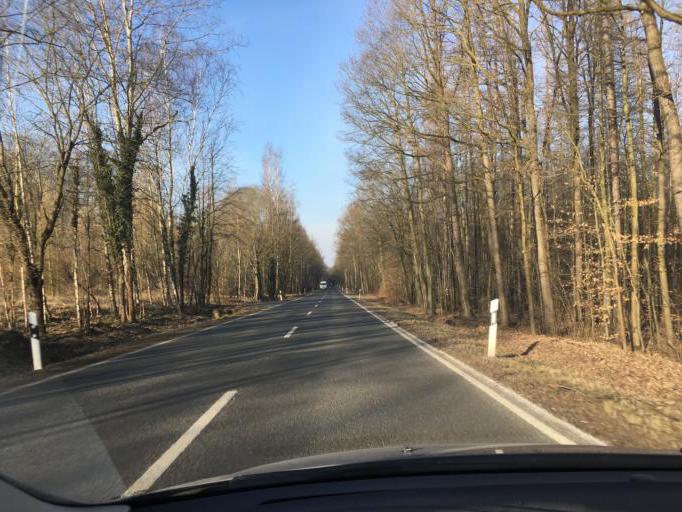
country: DE
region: Thuringia
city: Nobitz
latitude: 50.9831
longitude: 12.5302
